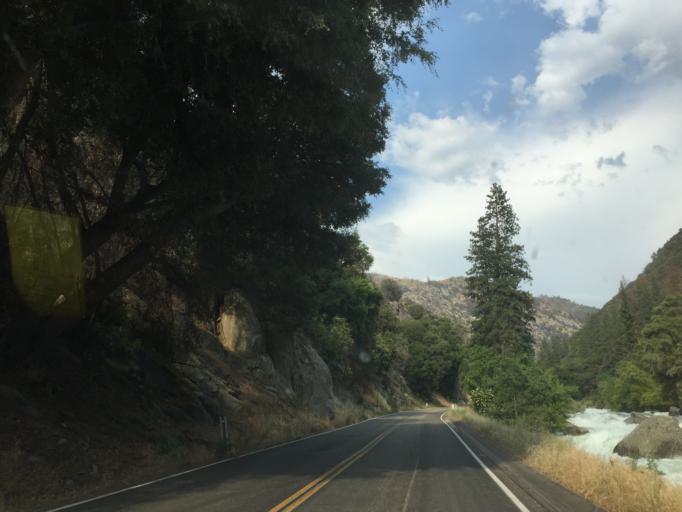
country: US
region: California
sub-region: Tulare County
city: Three Rivers
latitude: 36.8088
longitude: -118.7684
